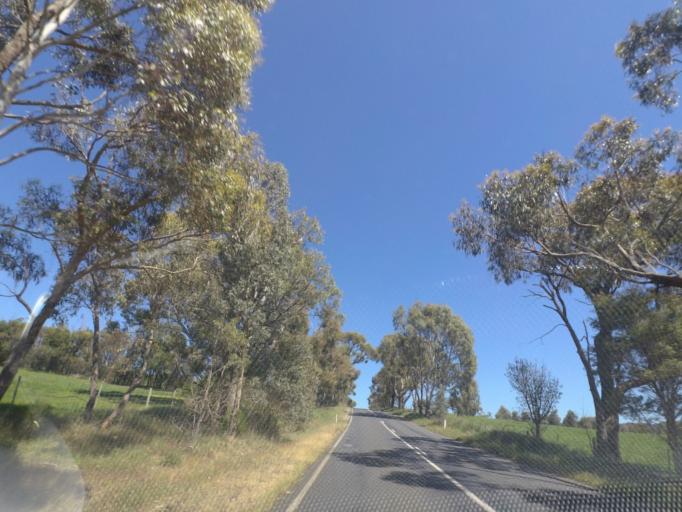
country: AU
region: Victoria
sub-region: Whittlesea
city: Whittlesea
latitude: -37.2658
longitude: 145.0384
